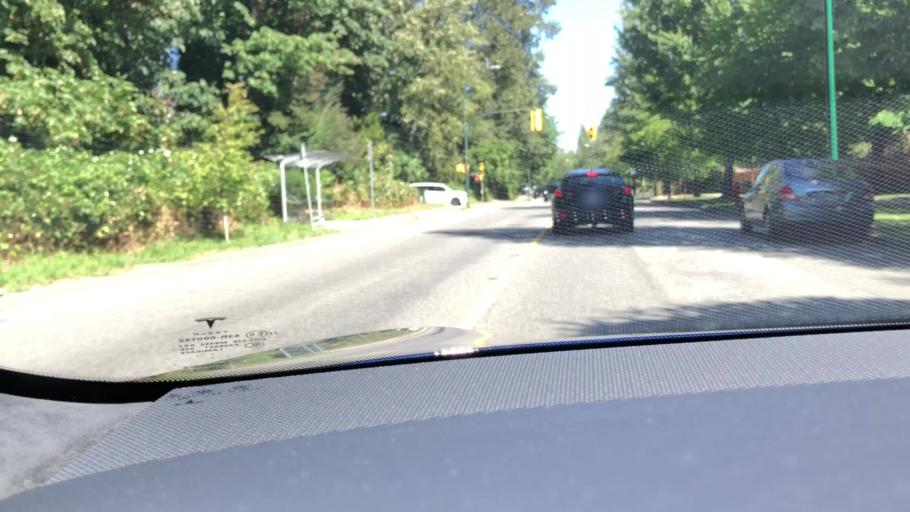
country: CA
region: British Columbia
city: Vancouver
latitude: 49.2083
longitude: -123.0318
